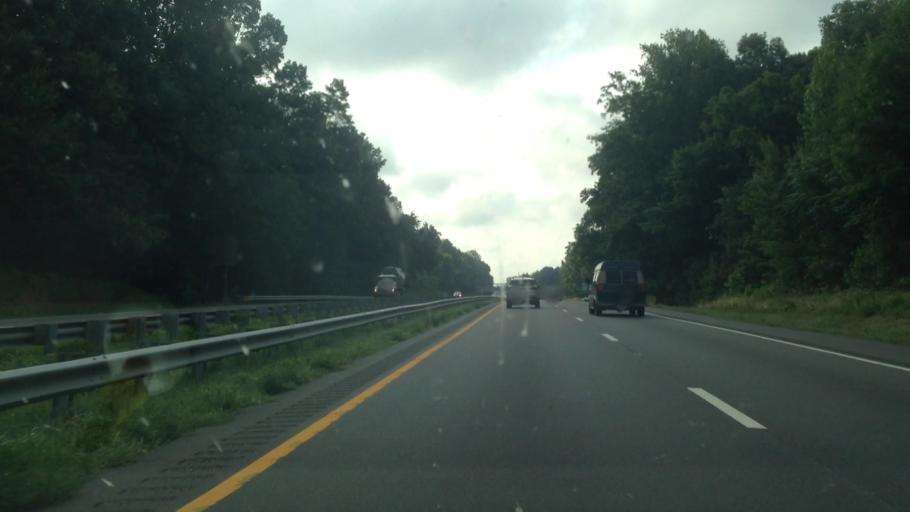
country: US
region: North Carolina
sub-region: Forsyth County
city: Kernersville
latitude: 36.1008
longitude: -80.0233
